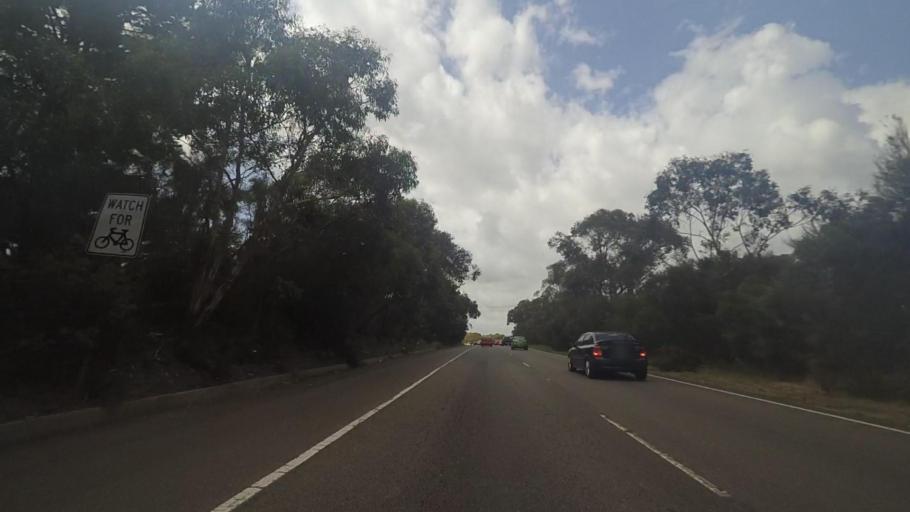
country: AU
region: New South Wales
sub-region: Sutherland Shire
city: Heathcote
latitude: -34.1199
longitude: 150.9919
